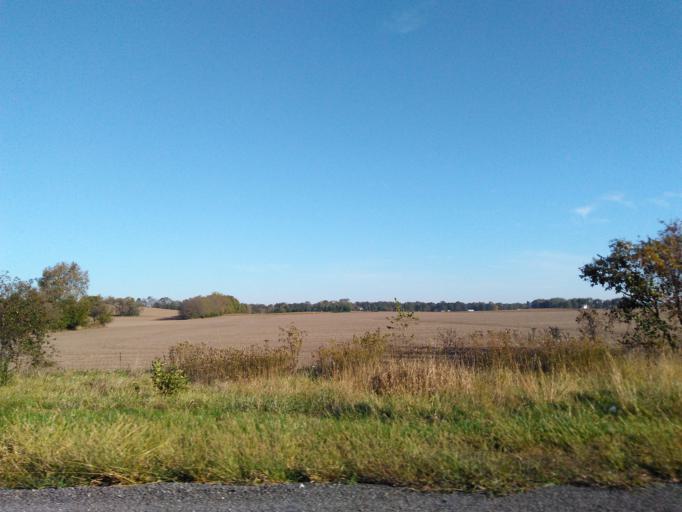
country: US
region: Illinois
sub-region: Madison County
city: Highland
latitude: 38.7869
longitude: -89.6794
